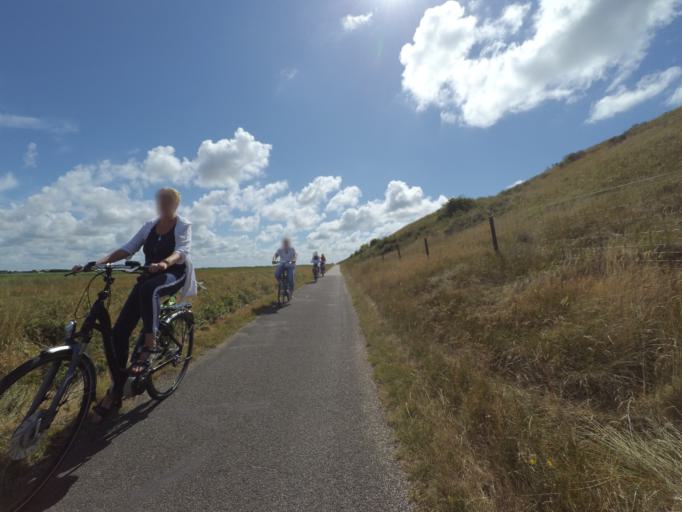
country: NL
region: North Holland
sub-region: Gemeente Texel
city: Den Burg
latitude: 53.1459
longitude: 4.8341
